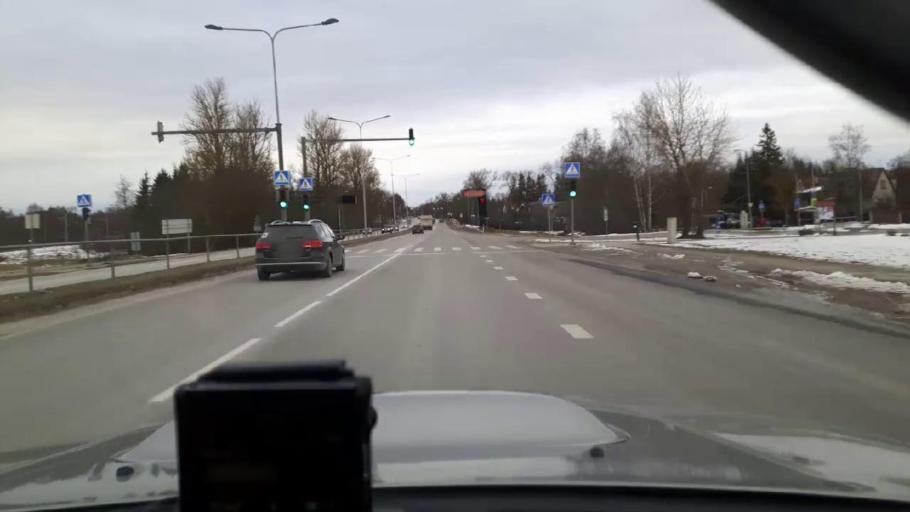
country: EE
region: Harju
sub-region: Saue vald
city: Laagri
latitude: 59.3509
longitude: 24.6280
